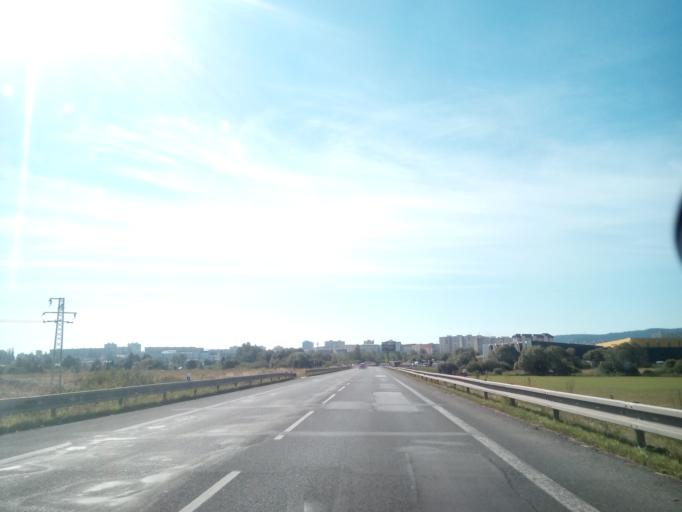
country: SK
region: Presovsky
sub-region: Okres Poprad
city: Poprad
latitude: 49.0546
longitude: 20.2767
